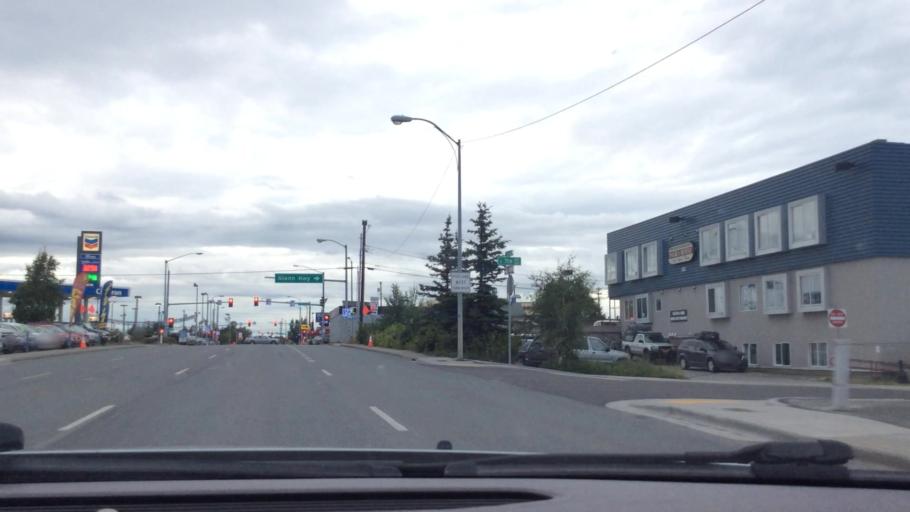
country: US
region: Alaska
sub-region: Anchorage Municipality
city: Anchorage
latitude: 61.2154
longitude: -149.8669
